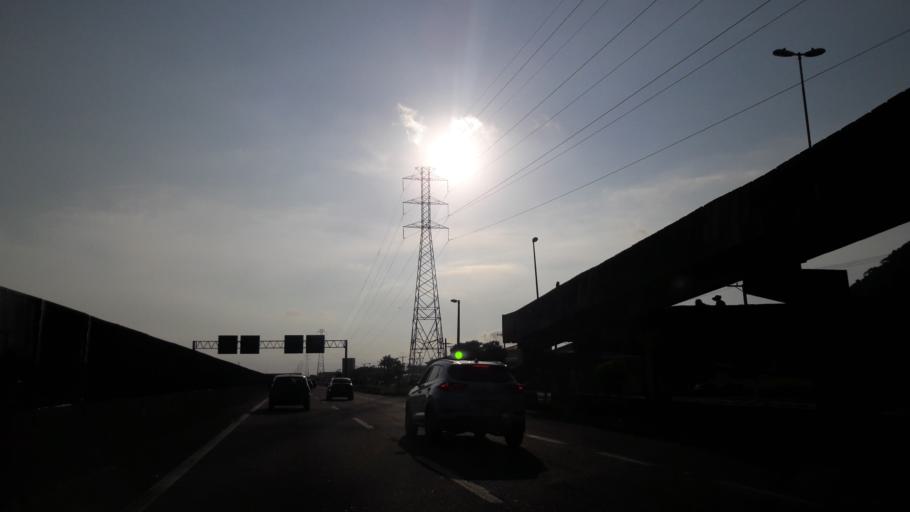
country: BR
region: Sao Paulo
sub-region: Mongagua
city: Mongagua
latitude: -24.1172
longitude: -46.6683
